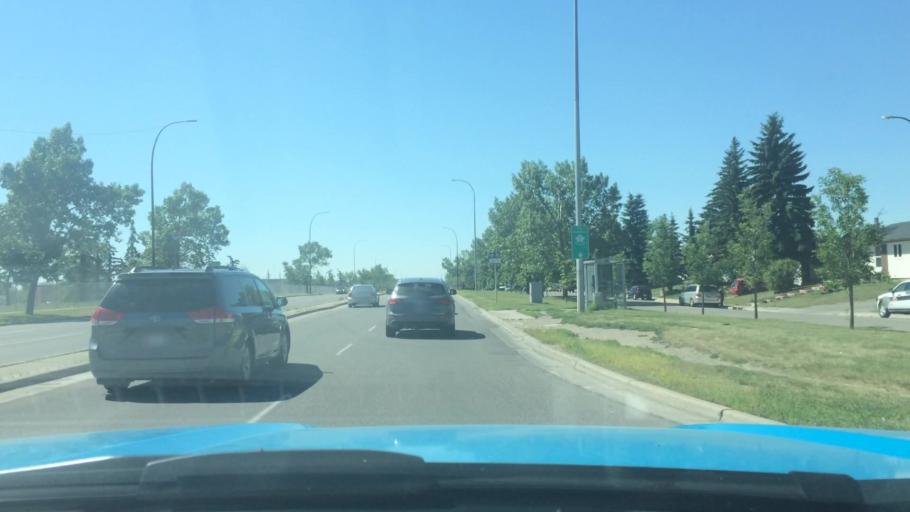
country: CA
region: Alberta
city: Calgary
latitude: 51.0813
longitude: -113.9584
